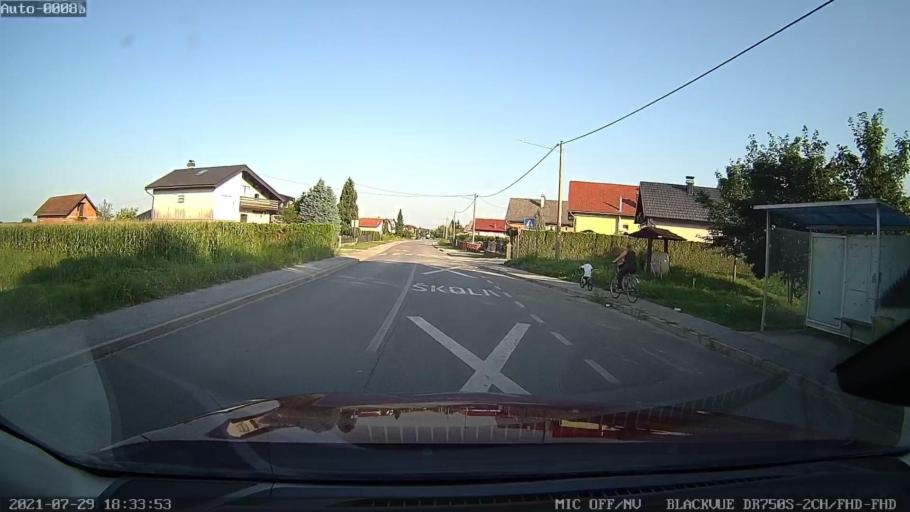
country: HR
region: Varazdinska
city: Vinica
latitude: 46.3132
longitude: 16.1615
